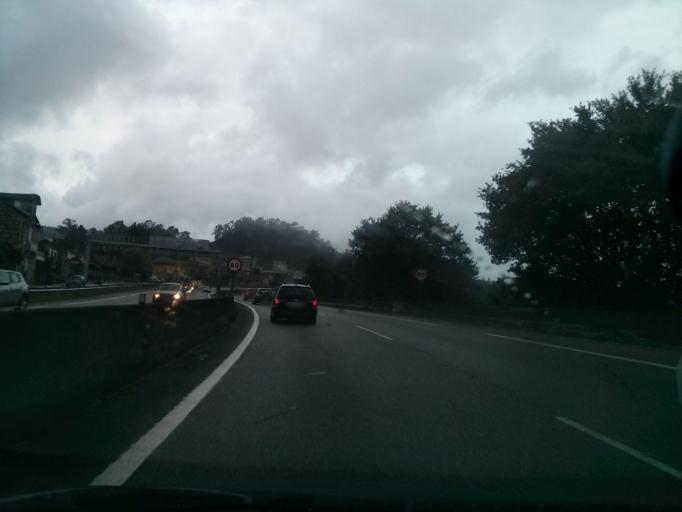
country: ES
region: Galicia
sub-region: Provincia de Pontevedra
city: Porrino
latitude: 42.1864
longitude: -8.6364
